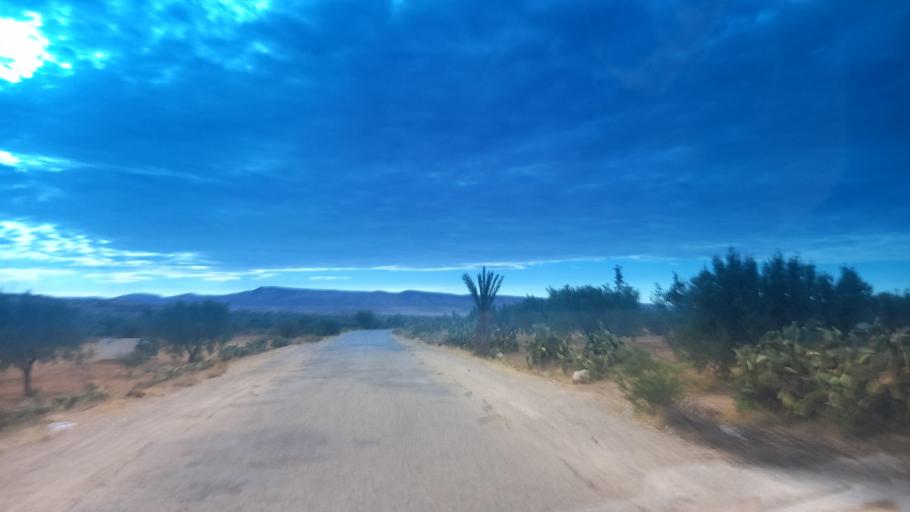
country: TN
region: Al Qasrayn
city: Sbiba
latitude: 35.3785
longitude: 9.0607
